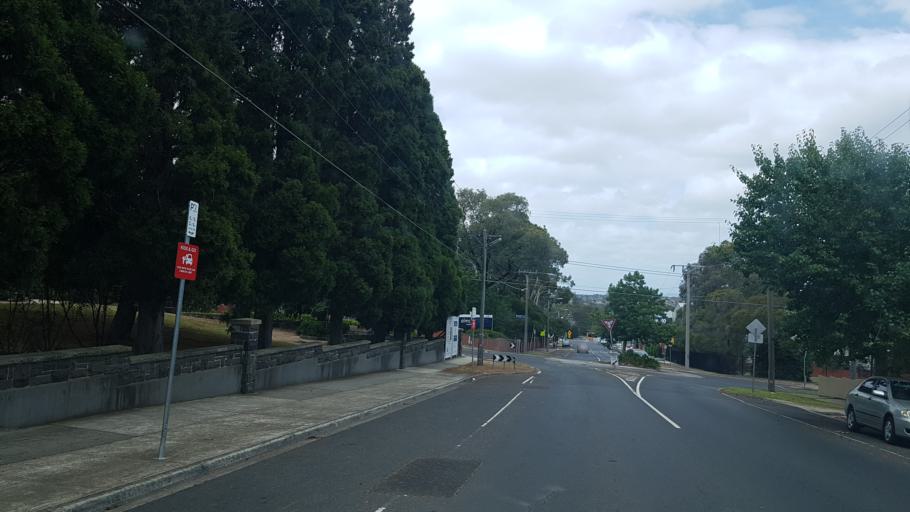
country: AU
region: Victoria
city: Rosanna
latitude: -37.7582
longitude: 145.0661
